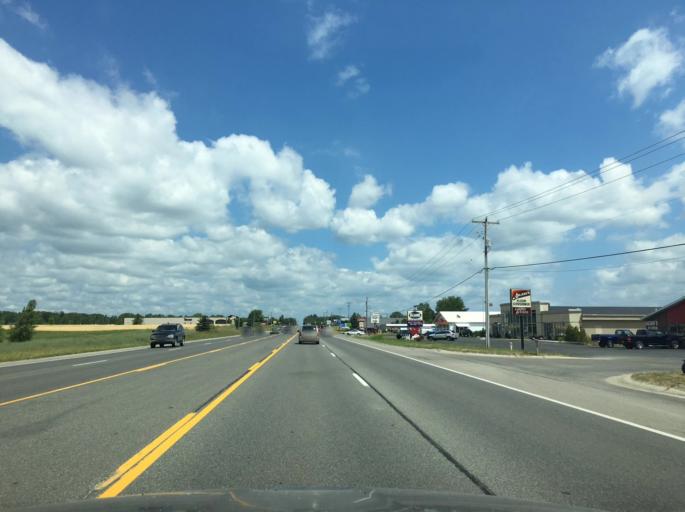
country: US
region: Michigan
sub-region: Grand Traverse County
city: Traverse City
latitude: 44.6919
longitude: -85.6562
